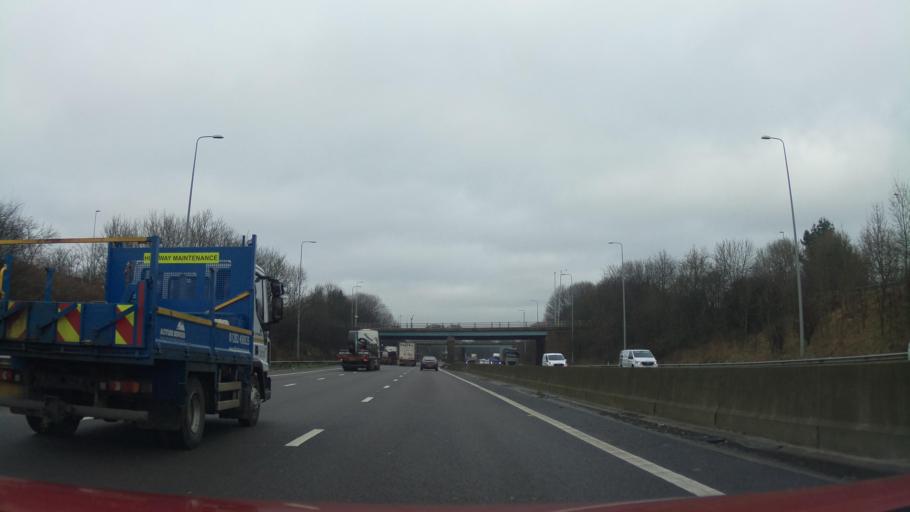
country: GB
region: England
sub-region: Borough of Wigan
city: Shevington
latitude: 53.5878
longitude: -2.6939
